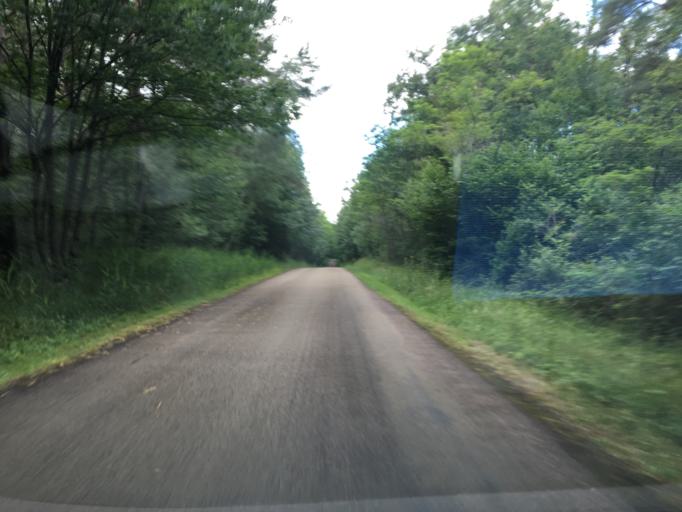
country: FR
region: Bourgogne
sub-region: Departement de l'Yonne
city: Charbuy
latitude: 47.8495
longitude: 3.4905
